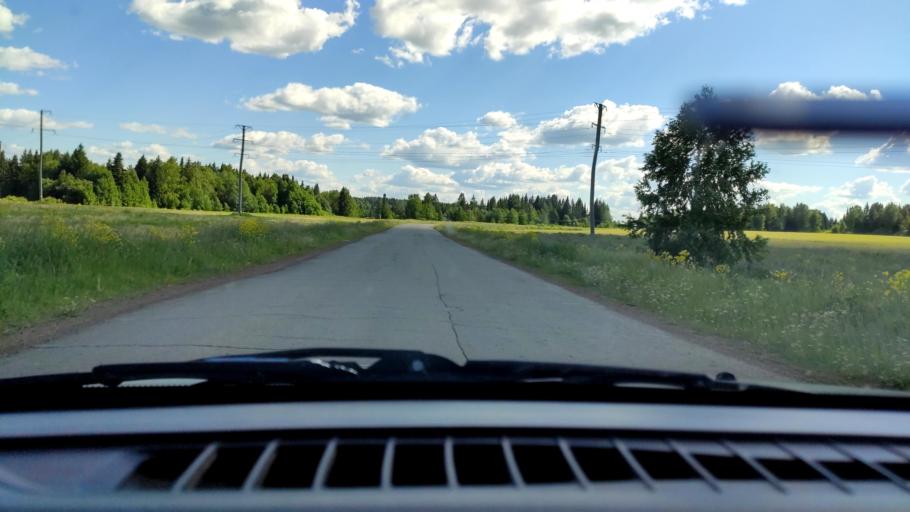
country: RU
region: Perm
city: Uinskoye
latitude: 57.1456
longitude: 56.5699
